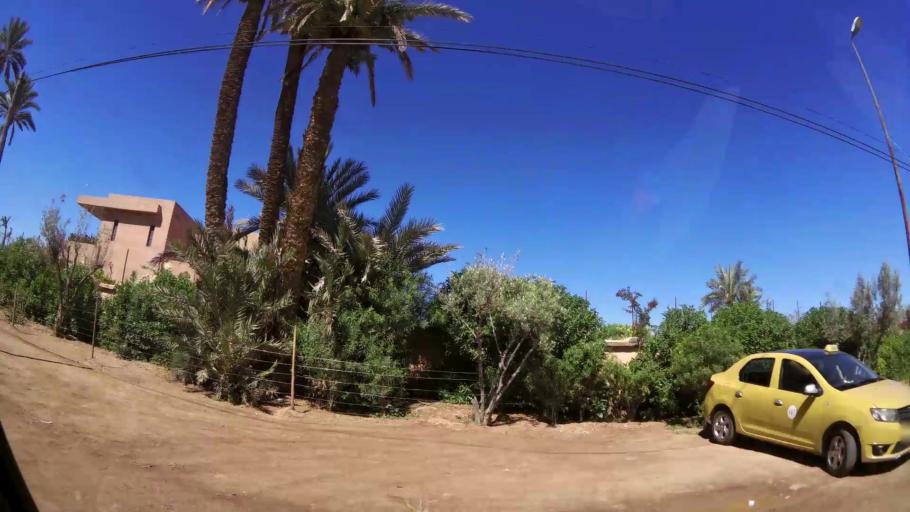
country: MA
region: Marrakech-Tensift-Al Haouz
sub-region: Marrakech
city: Marrakesh
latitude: 31.6794
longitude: -7.9722
